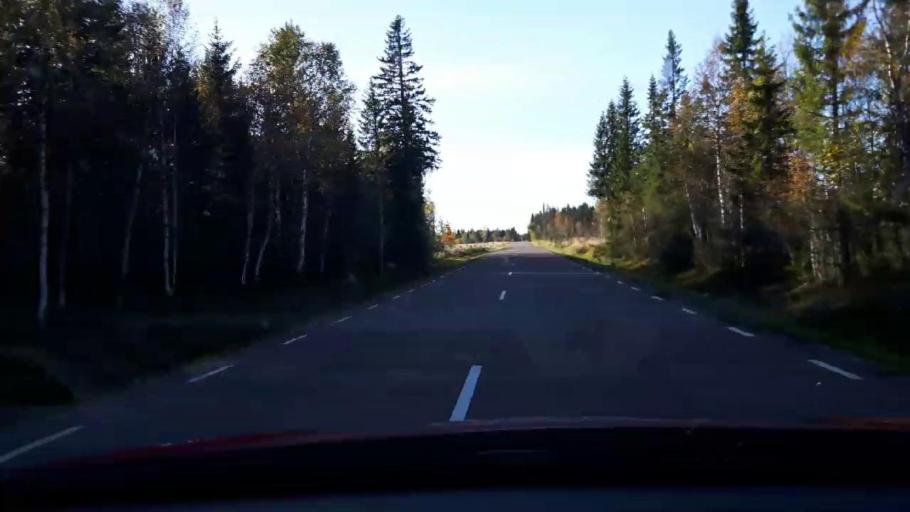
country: SE
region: Jaemtland
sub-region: Stroemsunds Kommun
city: Stroemsund
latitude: 63.8623
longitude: 15.1660
